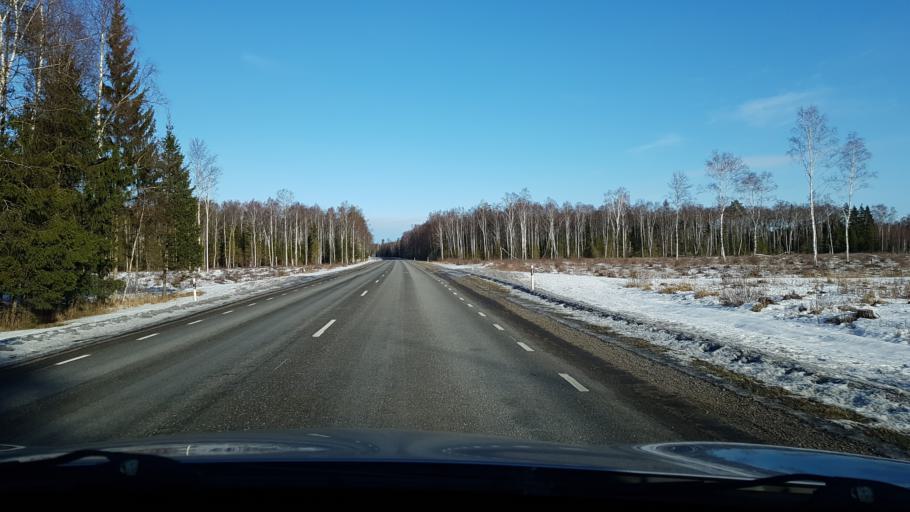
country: EE
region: Viljandimaa
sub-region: Vohma linn
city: Vohma
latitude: 58.5952
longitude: 25.5722
